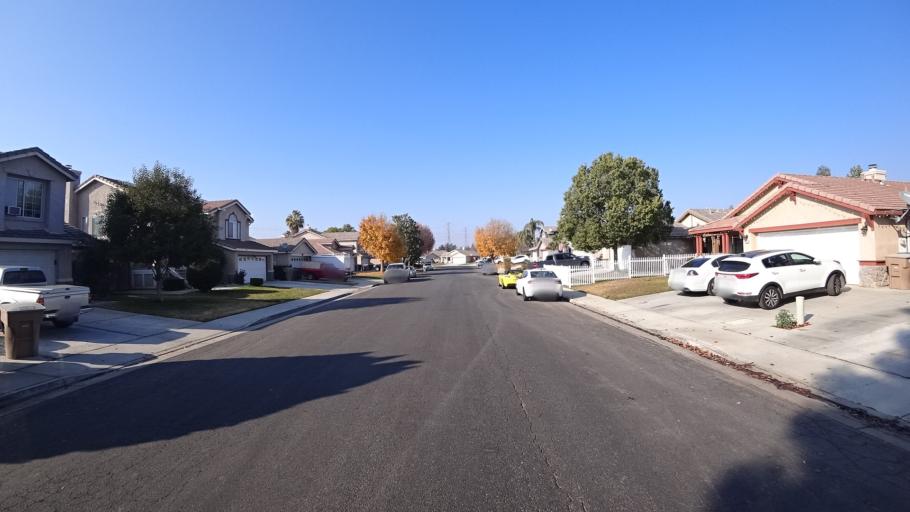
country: US
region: California
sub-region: Kern County
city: Greenacres
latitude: 35.3224
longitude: -119.0941
